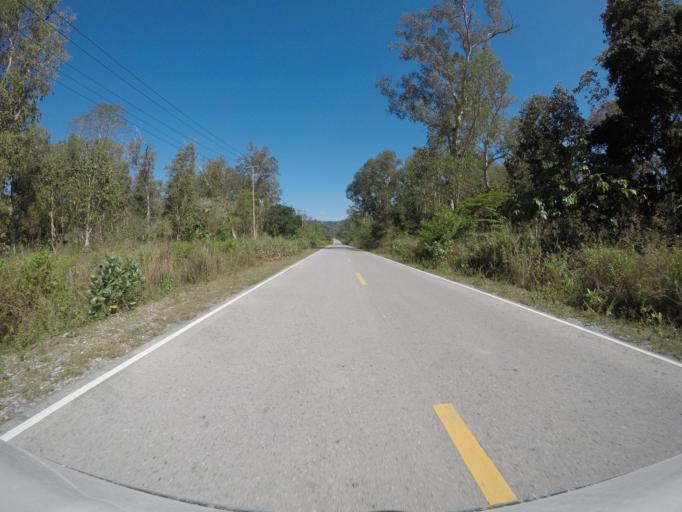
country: TL
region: Viqueque
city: Viqueque
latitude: -8.9617
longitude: 126.0145
